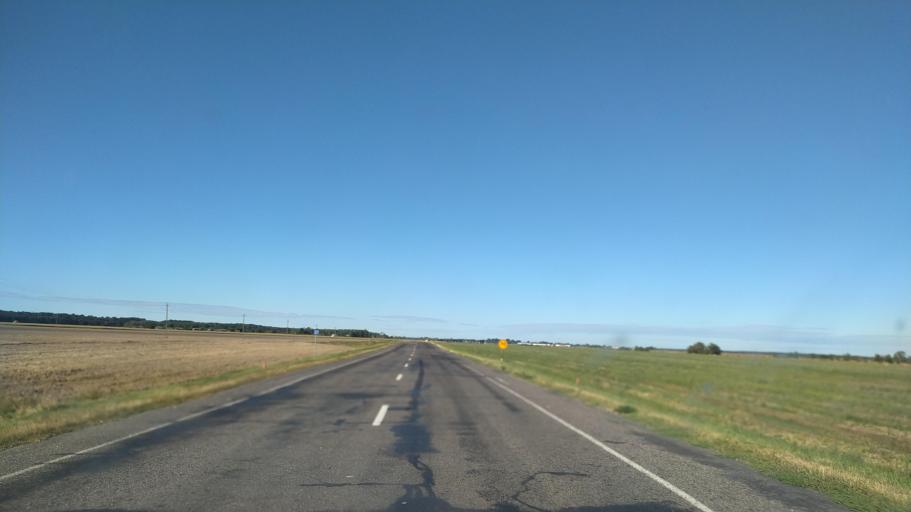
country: BY
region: Brest
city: Byaroza
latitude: 52.5024
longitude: 24.8339
